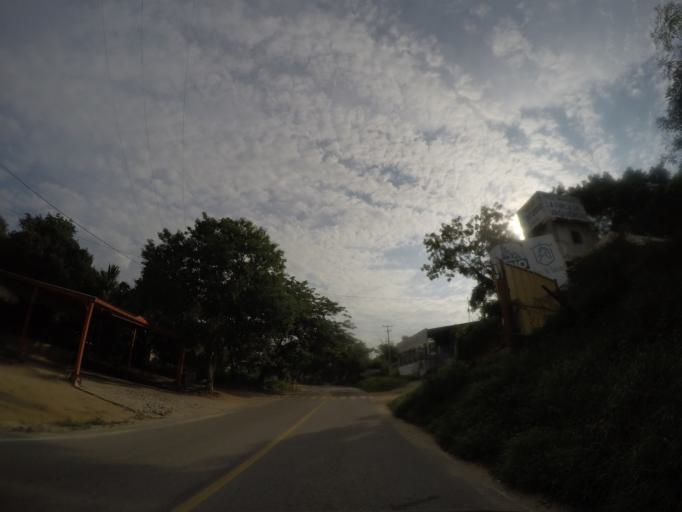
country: MX
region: Oaxaca
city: San Pedro Pochutla
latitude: 15.7148
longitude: -96.4795
